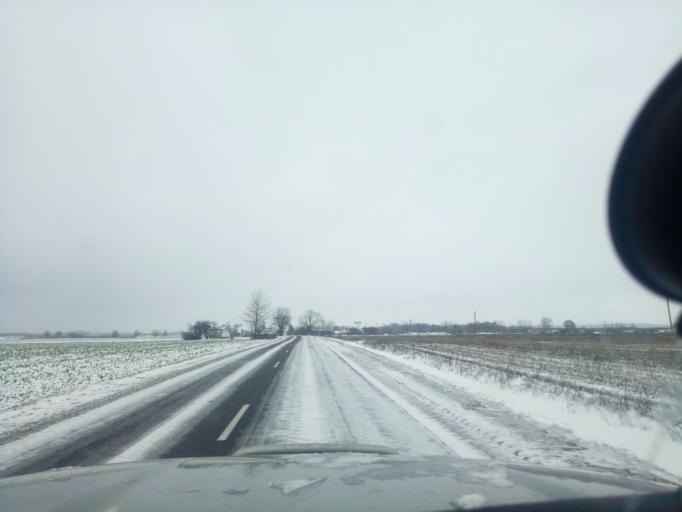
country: BY
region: Minsk
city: Klyetsk
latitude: 53.0524
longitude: 26.7666
